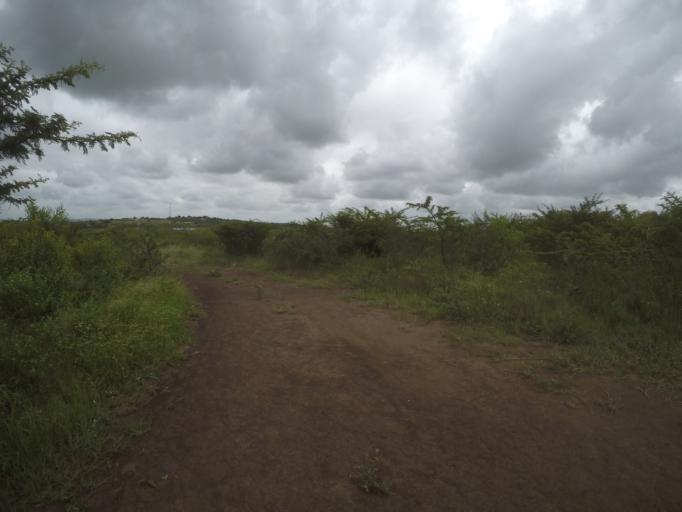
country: ZA
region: KwaZulu-Natal
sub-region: uThungulu District Municipality
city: Empangeni
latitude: -28.5587
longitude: 31.8849
